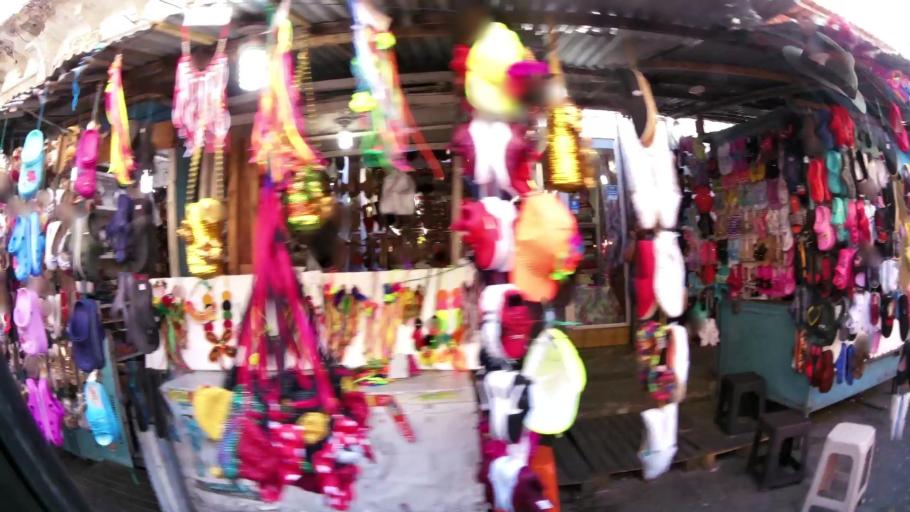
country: CO
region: Atlantico
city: Barranquilla
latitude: 10.9802
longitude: -74.7795
